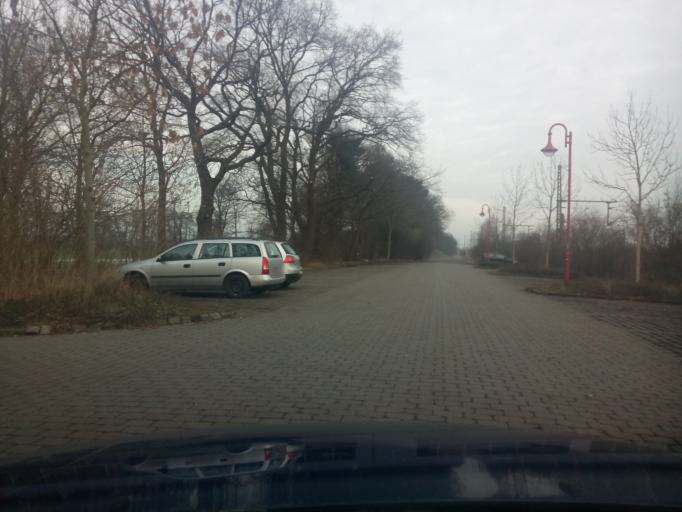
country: DE
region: Lower Saxony
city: Oyten
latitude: 53.0846
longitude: 9.0246
